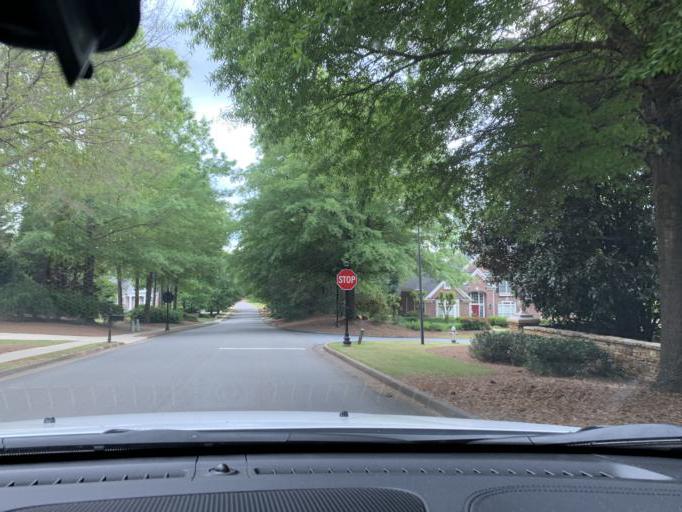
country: US
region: Georgia
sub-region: Gwinnett County
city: Suwanee
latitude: 34.1084
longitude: -84.1128
